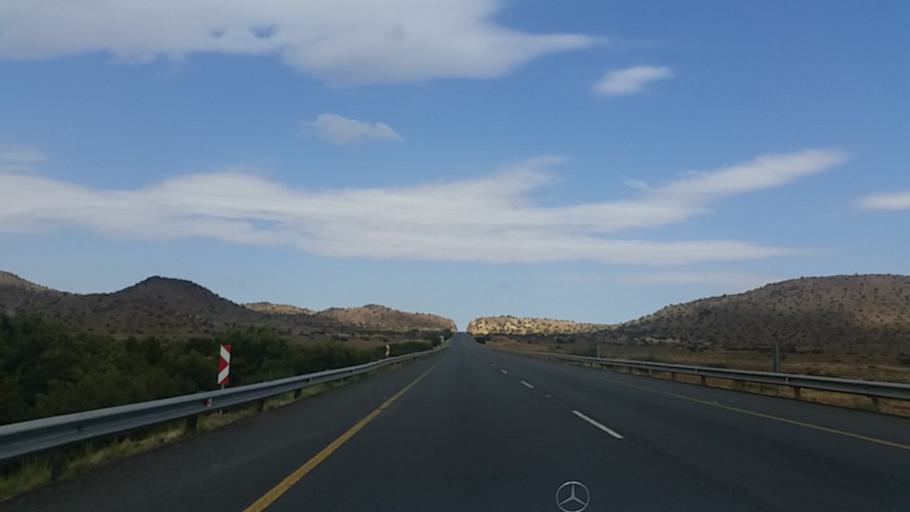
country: ZA
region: Northern Cape
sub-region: Pixley ka Seme District Municipality
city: Colesberg
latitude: -30.6388
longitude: 25.2306
